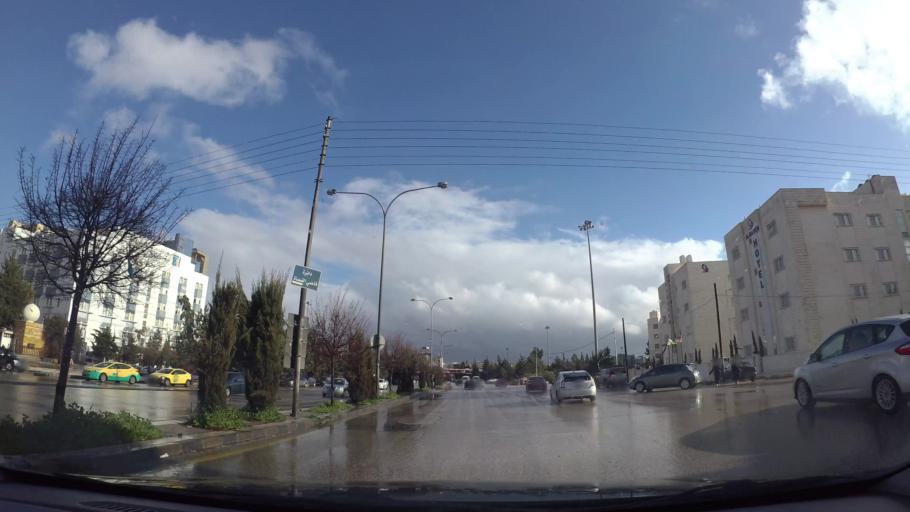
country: JO
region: Amman
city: Al Jubayhah
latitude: 32.0047
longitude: 35.8735
